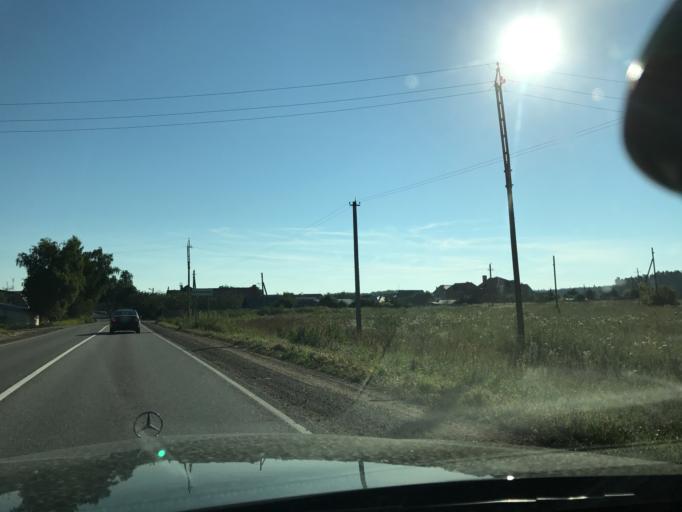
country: RU
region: Moskovskaya
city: Bakhchivandzhi
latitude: 55.8537
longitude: 38.1243
